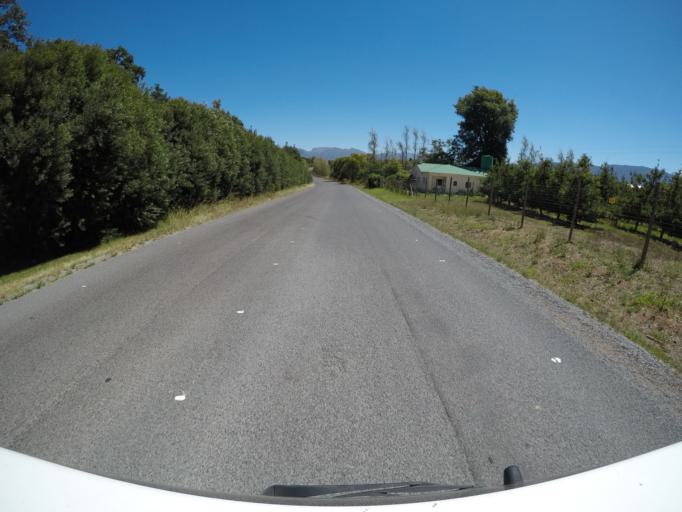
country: ZA
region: Western Cape
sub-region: Overberg District Municipality
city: Grabouw
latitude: -34.1879
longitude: 19.0397
